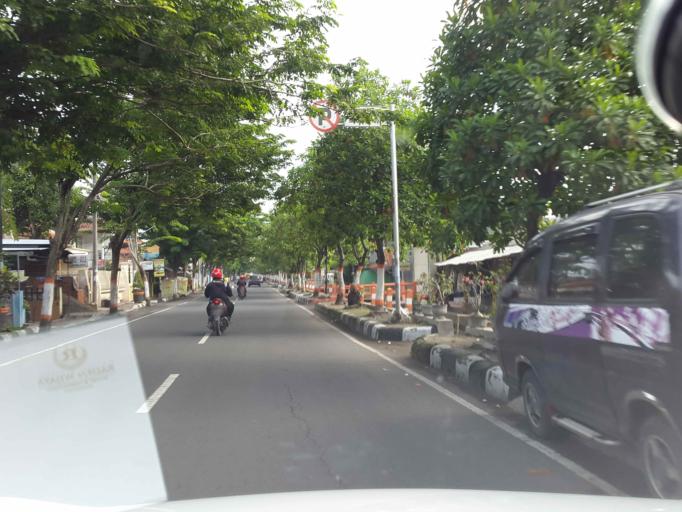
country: ID
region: East Java
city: Soko
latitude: -7.4768
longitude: 112.4290
